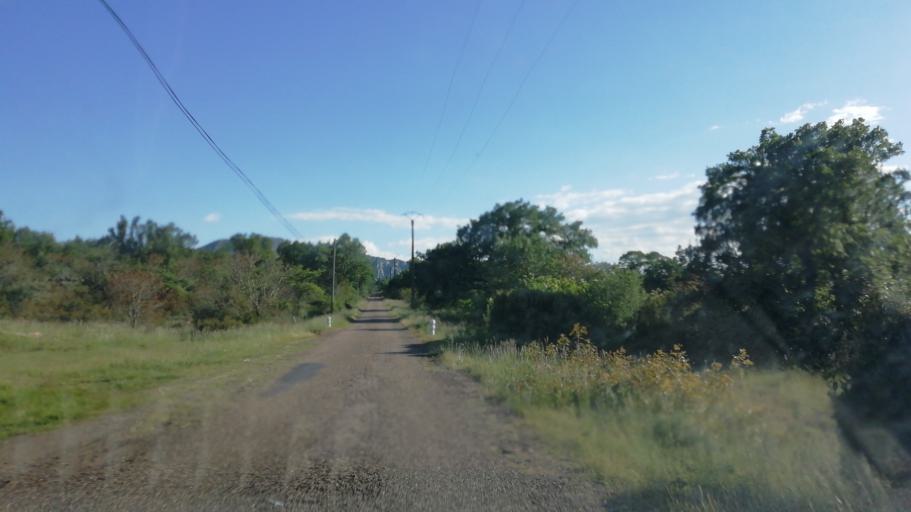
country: FR
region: Languedoc-Roussillon
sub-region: Departement de l'Herault
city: Saint-Mathieu-de-Treviers
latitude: 43.8163
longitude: 3.8139
